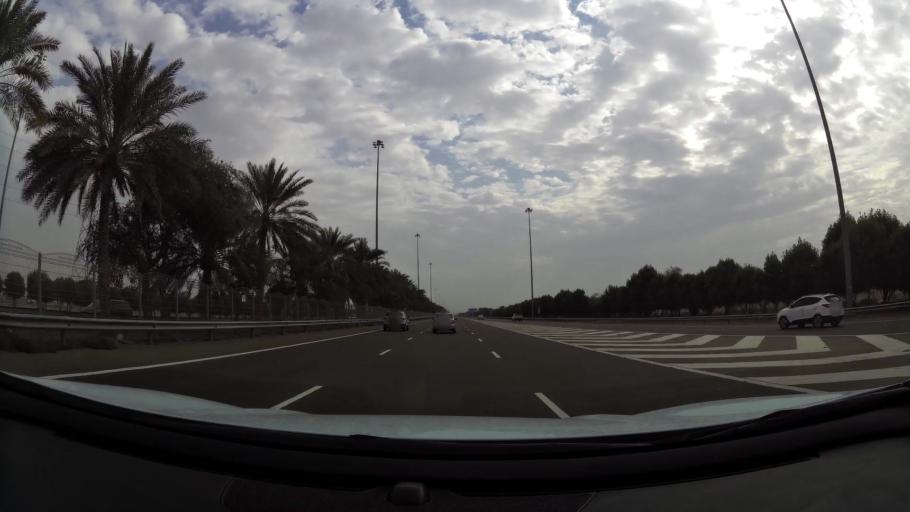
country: AE
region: Abu Dhabi
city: Al Ain
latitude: 24.2138
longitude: 55.5260
